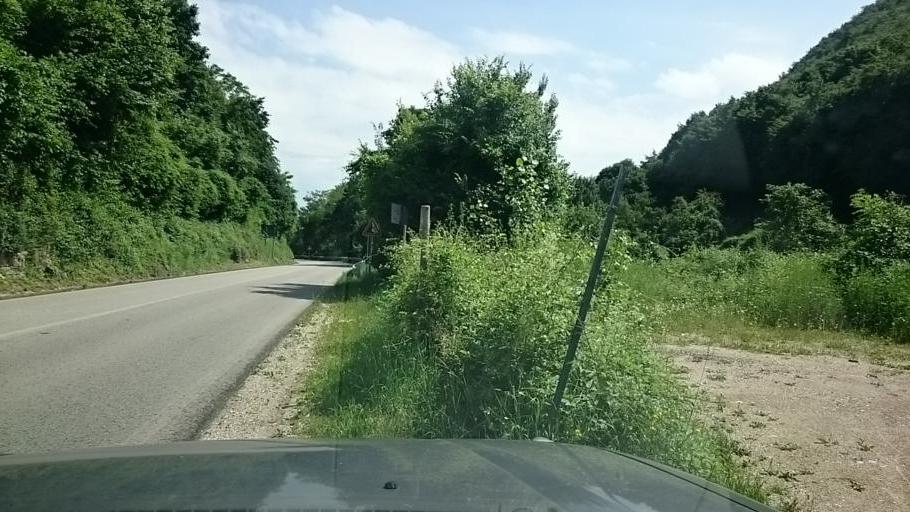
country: IT
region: Veneto
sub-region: Provincia di Vicenza
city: Conco
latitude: 45.7840
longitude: 11.5990
